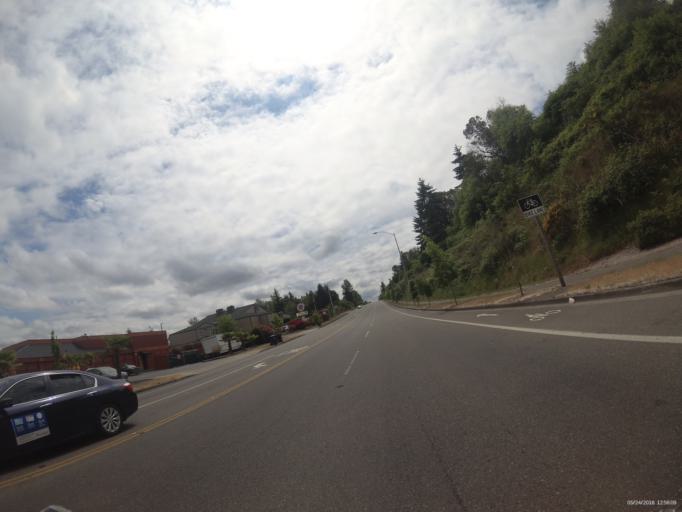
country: US
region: Washington
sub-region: Pierce County
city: Fircrest
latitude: 47.2059
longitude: -122.4932
